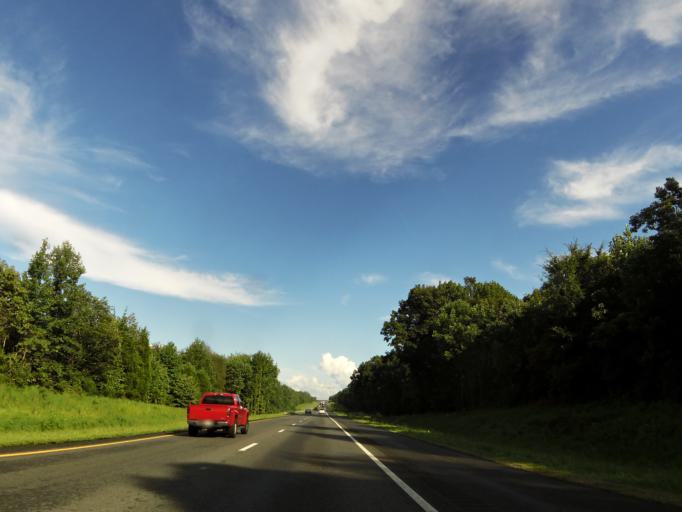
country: US
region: Tennessee
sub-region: Cheatham County
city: Pleasant View
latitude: 36.4833
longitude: -87.1540
